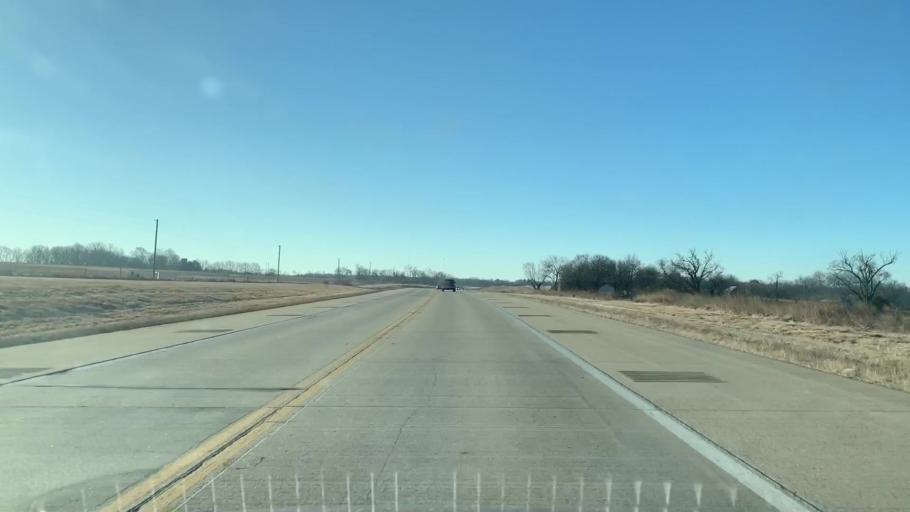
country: US
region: Kansas
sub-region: Crawford County
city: Arma
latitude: 37.5771
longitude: -94.7054
